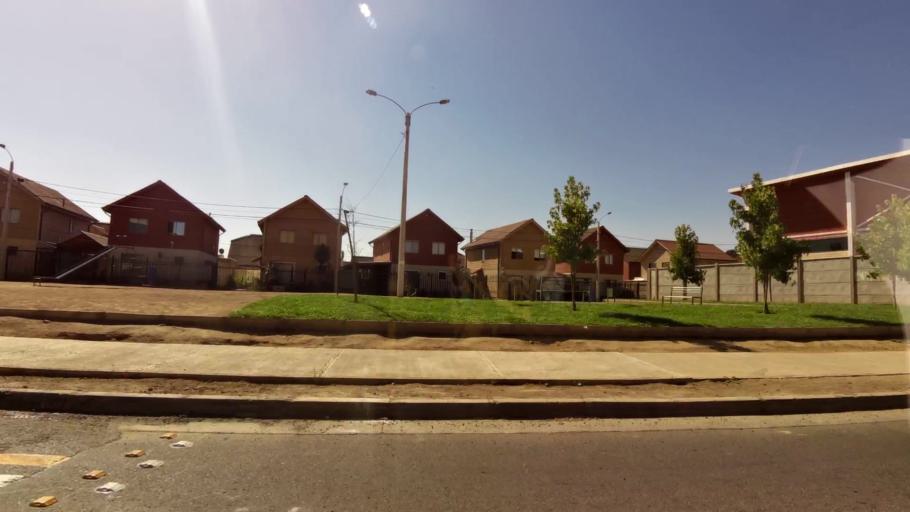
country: CL
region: Maule
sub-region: Provincia de Talca
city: Talca
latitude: -35.4146
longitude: -71.6157
